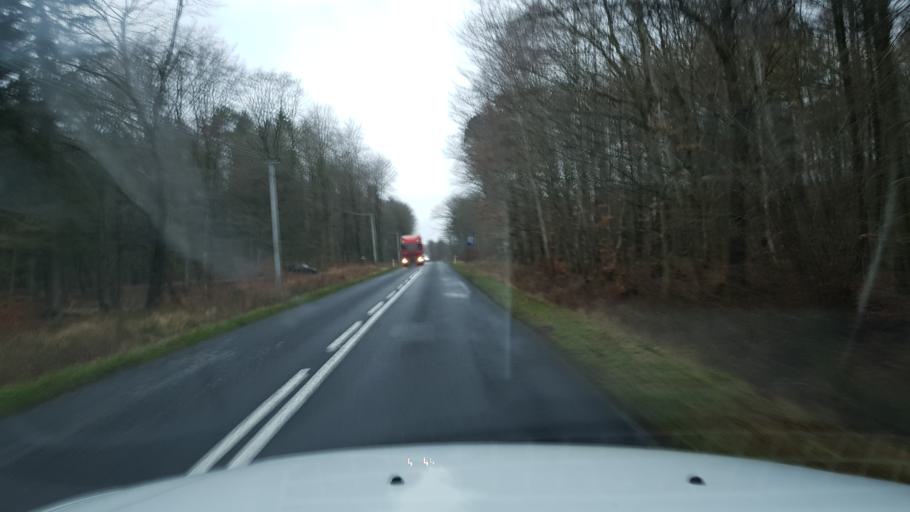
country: PL
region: West Pomeranian Voivodeship
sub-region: Powiat gryficki
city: Trzebiatow
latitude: 54.0575
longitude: 15.3358
